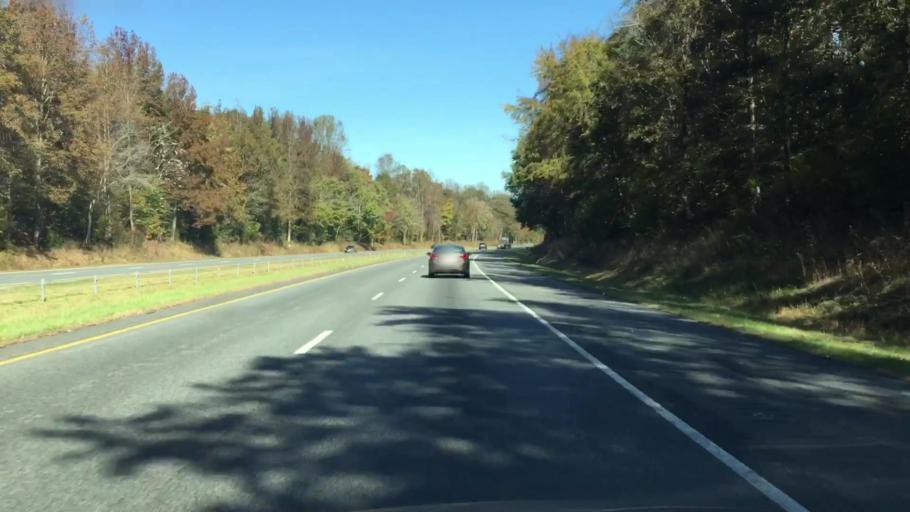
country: US
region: North Carolina
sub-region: Rockingham County
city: Reidsville
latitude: 36.2916
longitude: -79.6415
